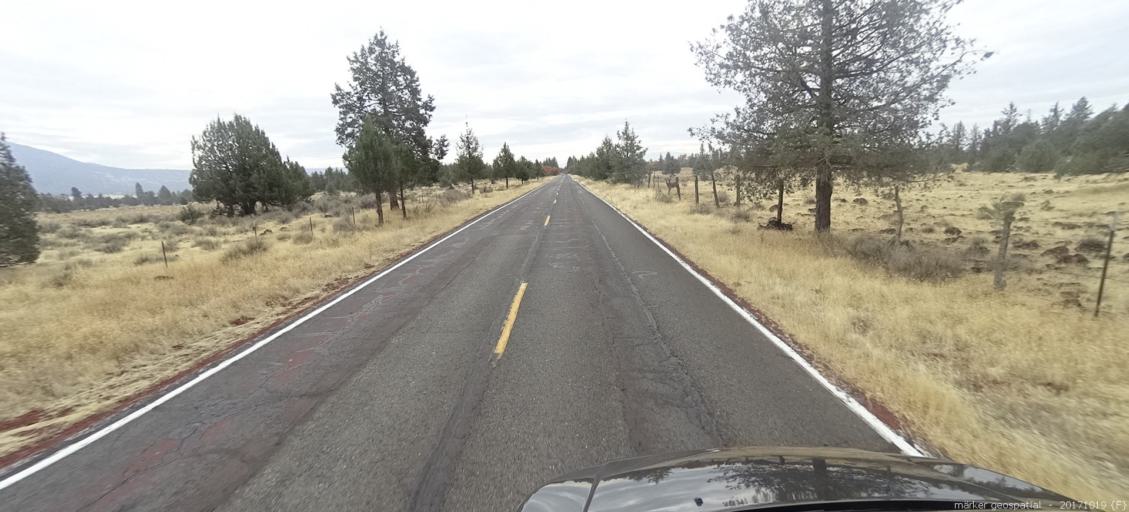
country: US
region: California
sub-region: Shasta County
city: Burney
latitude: 41.1008
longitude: -121.3233
